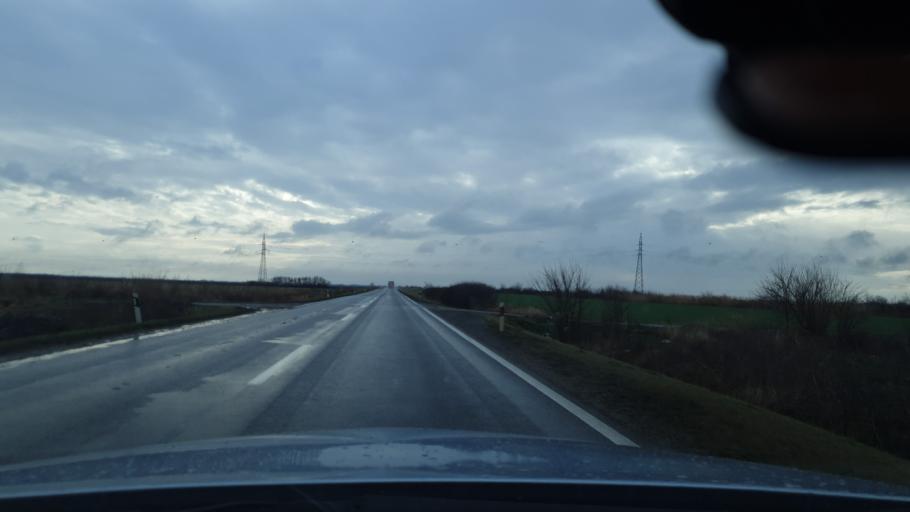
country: RS
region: Autonomna Pokrajina Vojvodina
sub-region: Juznobanatski Okrug
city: Kovin
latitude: 44.7980
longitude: 20.9065
